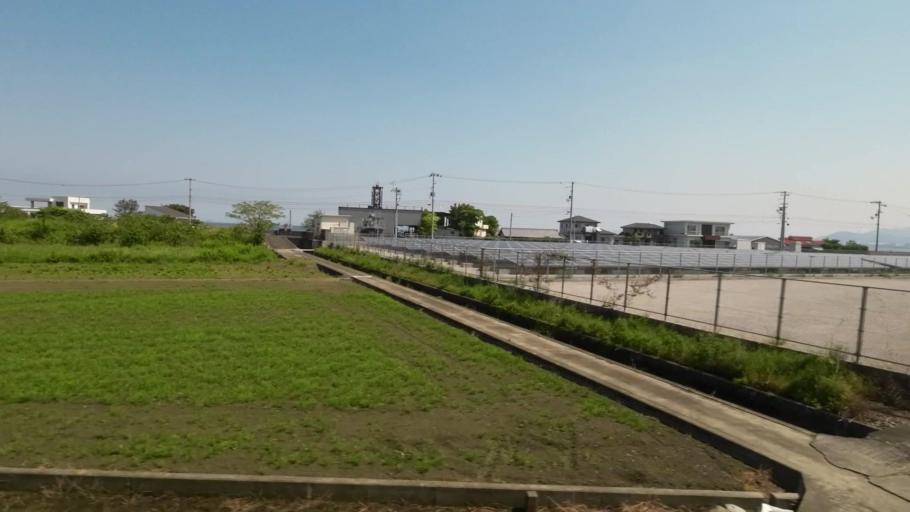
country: JP
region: Ehime
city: Kawanoecho
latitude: 33.9679
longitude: 133.4896
